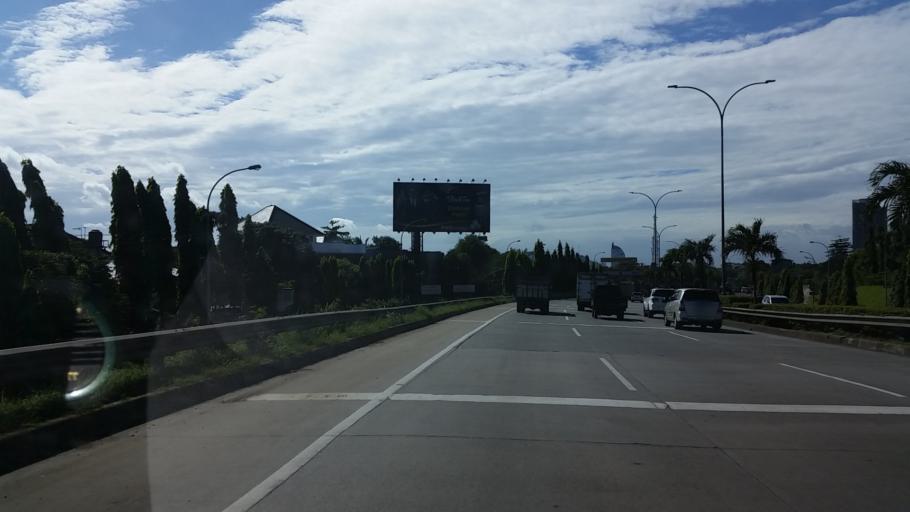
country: ID
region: Banten
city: South Tangerang
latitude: -6.2626
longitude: 106.7675
